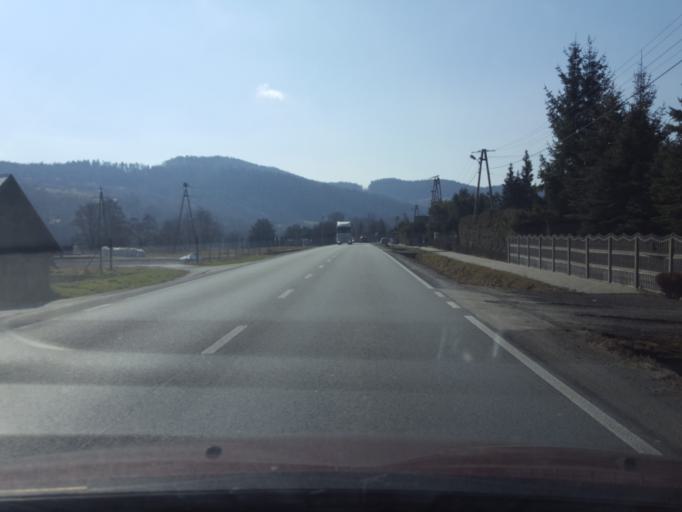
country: PL
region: Lesser Poland Voivodeship
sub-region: Powiat brzeski
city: Czchow
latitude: 49.8219
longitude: 20.6803
